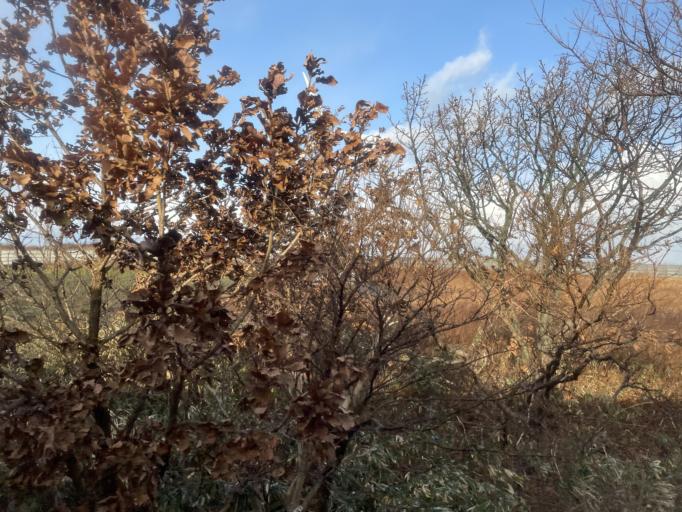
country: JP
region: Aomori
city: Misawa
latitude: 40.9086
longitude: 141.1847
